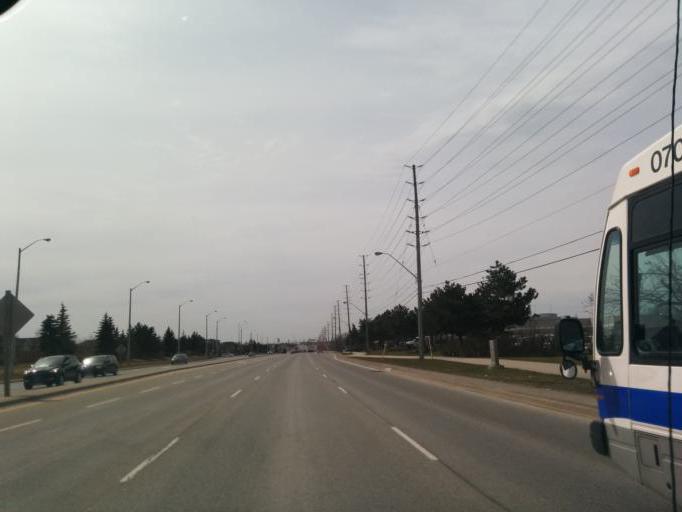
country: CA
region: Ontario
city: Brampton
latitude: 43.7002
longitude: -79.7929
